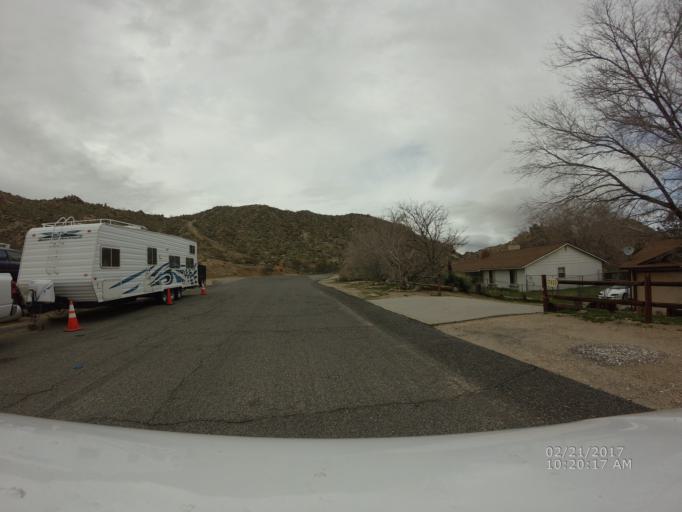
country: US
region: California
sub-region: Los Angeles County
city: Lake Los Angeles
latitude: 34.6074
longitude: -117.8167
